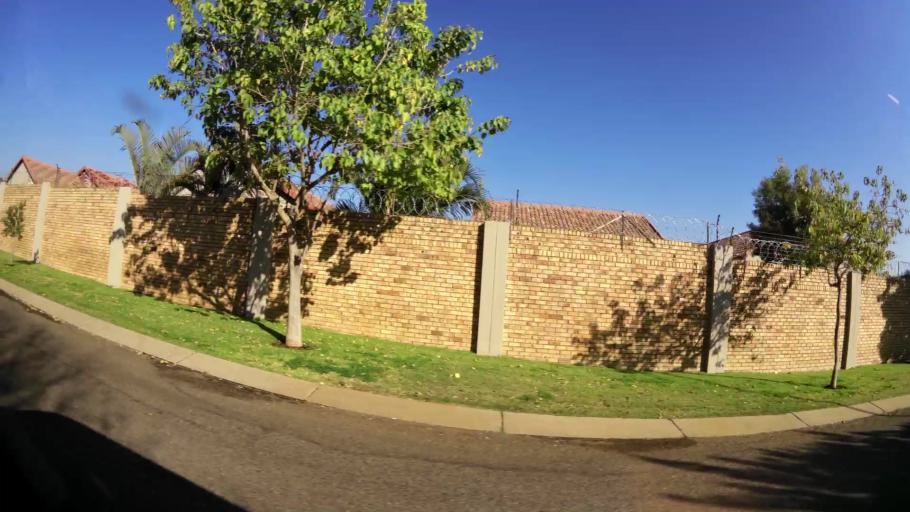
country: ZA
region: Gauteng
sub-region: City of Tshwane Metropolitan Municipality
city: Pretoria
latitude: -25.6805
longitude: 28.2276
